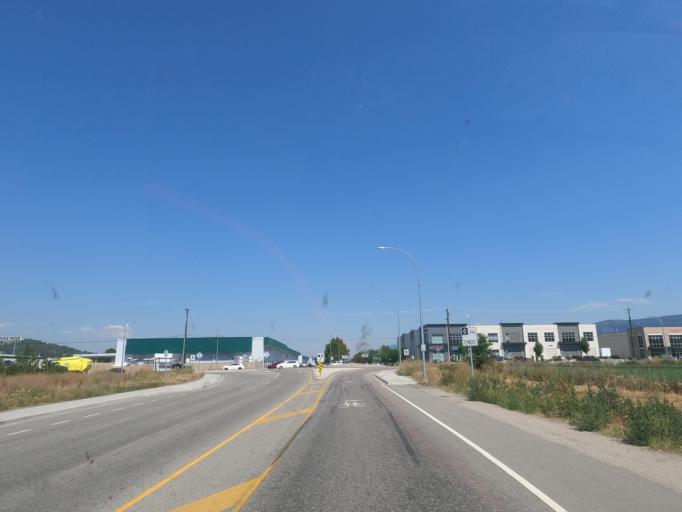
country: CA
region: British Columbia
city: Kelowna
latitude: 49.9174
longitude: -119.3841
